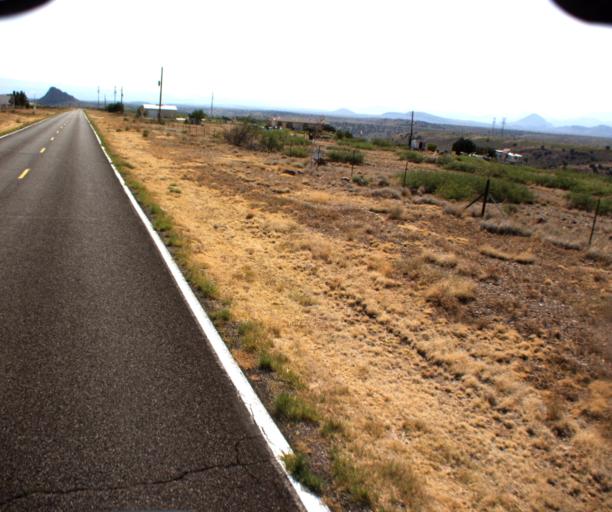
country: US
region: Arizona
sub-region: Greenlee County
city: Clifton
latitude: 33.0401
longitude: -109.1210
